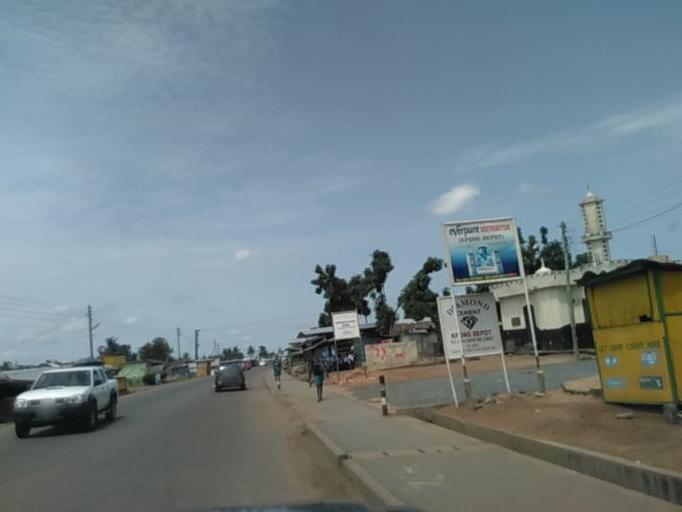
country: GH
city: Akropong
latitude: 6.1605
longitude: 0.0638
